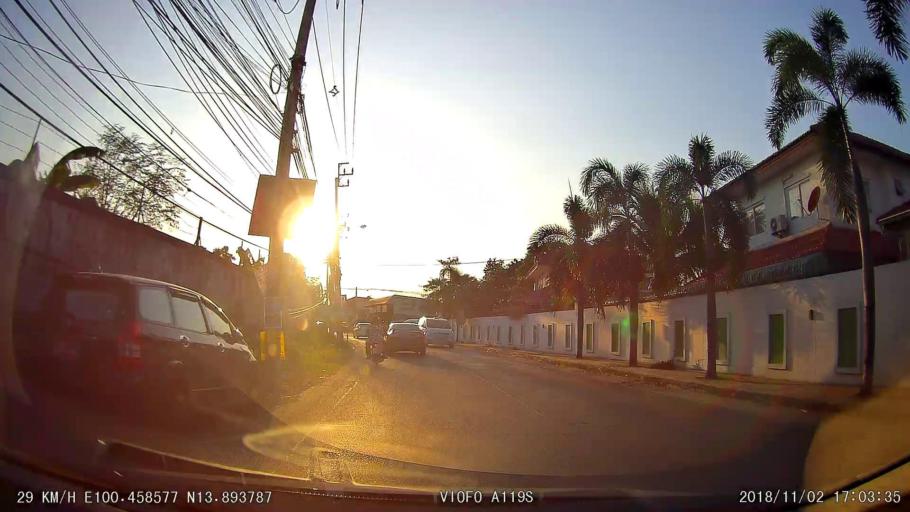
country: TH
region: Nonthaburi
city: Bang Bua Thong
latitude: 13.8938
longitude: 100.4585
